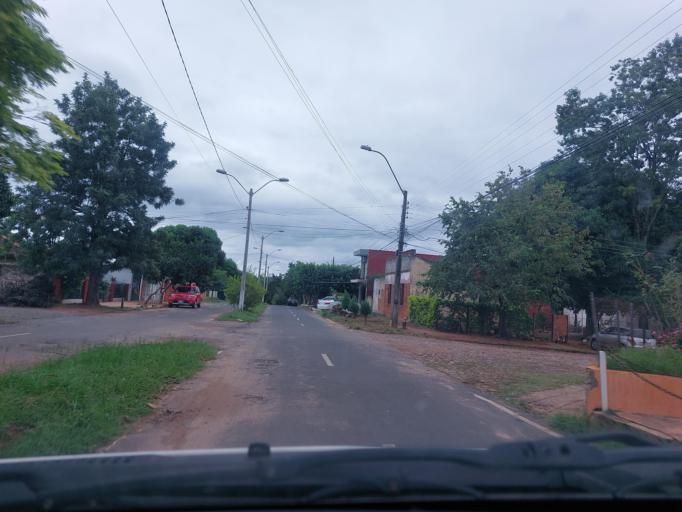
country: PY
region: San Pedro
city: Guayaybi
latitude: -24.6607
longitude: -56.4411
